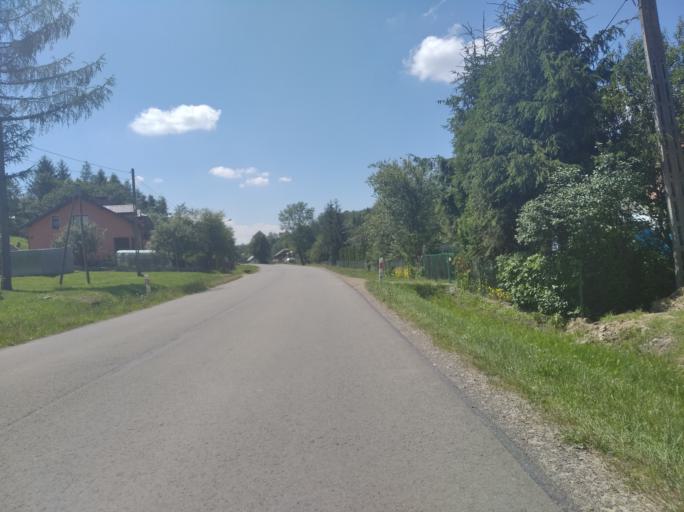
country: PL
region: Subcarpathian Voivodeship
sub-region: Powiat brzozowski
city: Jablonka
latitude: 49.6981
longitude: 22.1195
